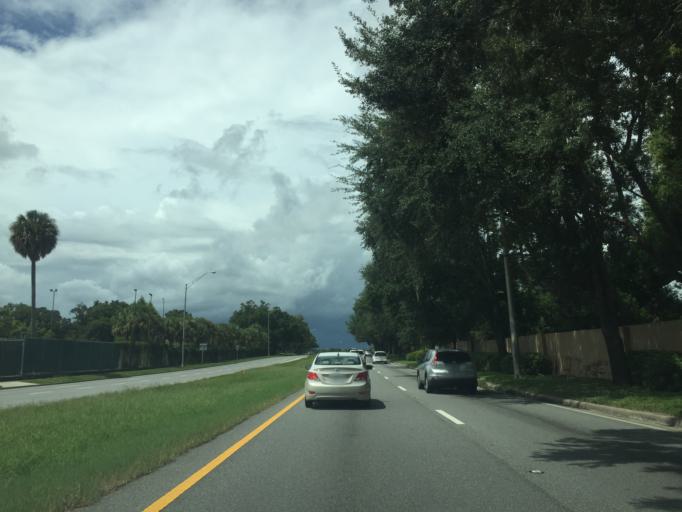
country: US
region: Florida
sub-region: Orange County
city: Maitland
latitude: 28.6362
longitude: -81.3670
